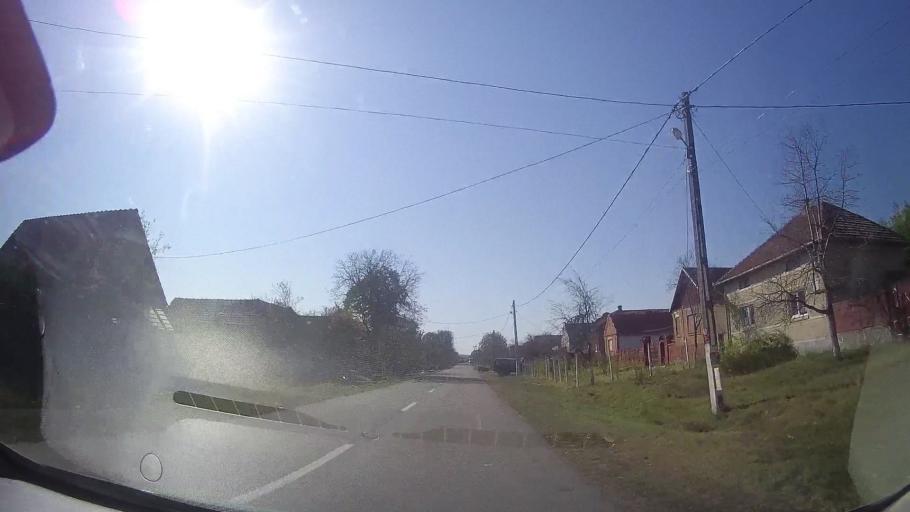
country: RO
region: Timis
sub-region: Comuna Secas
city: Secas
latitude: 45.8505
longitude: 21.7933
